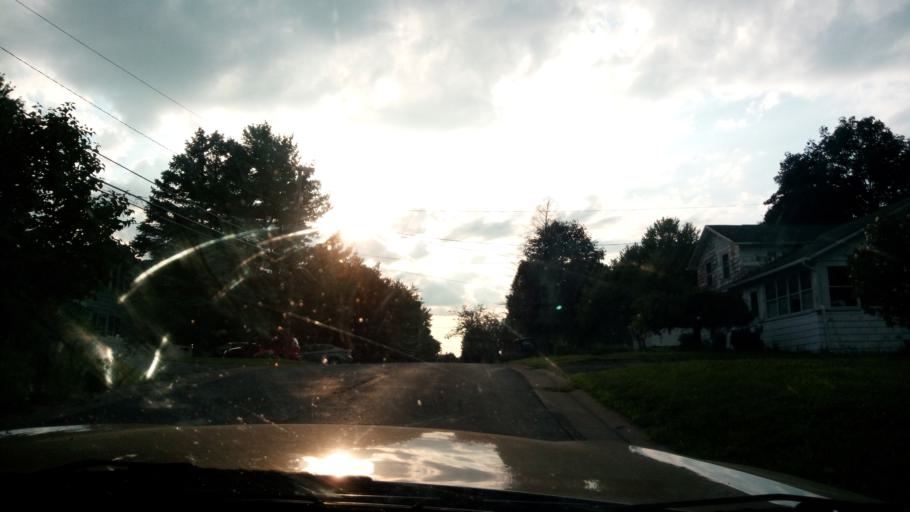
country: US
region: New York
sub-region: Wayne County
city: Clyde
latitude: 43.0878
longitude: -76.8736
